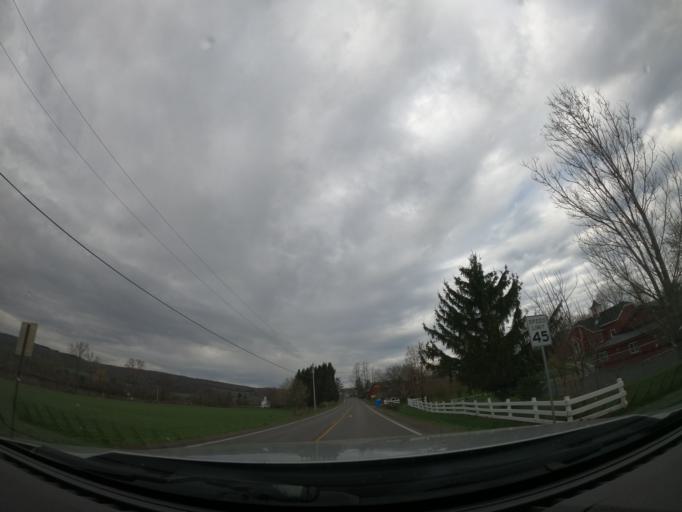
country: US
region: New York
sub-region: Madison County
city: Cazenovia
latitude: 42.8135
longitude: -75.8274
